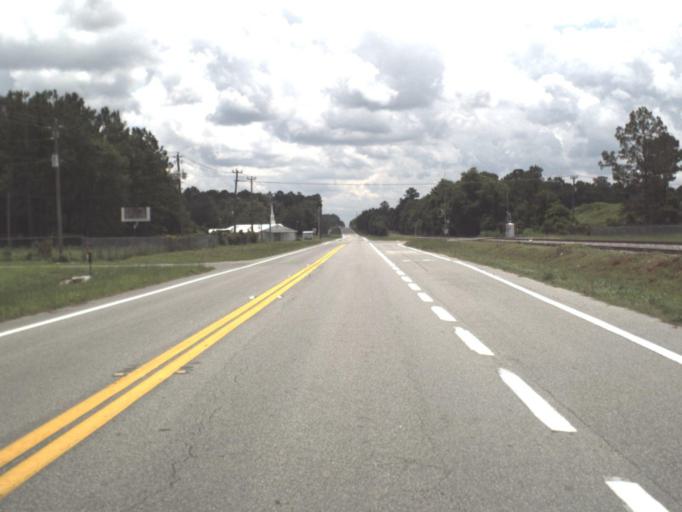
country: US
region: Florida
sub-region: Columbia County
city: Watertown
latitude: 30.1697
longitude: -82.5800
